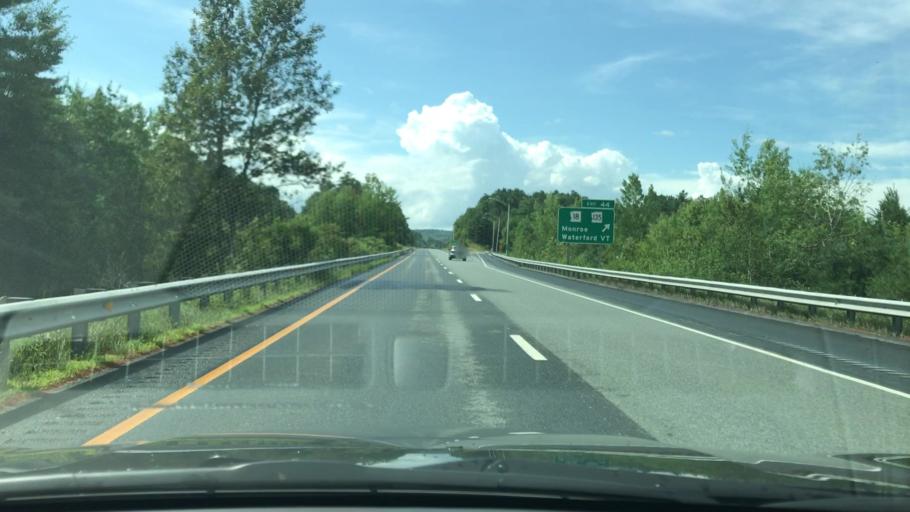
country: US
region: New Hampshire
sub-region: Grafton County
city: Littleton
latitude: 44.3286
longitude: -71.8720
